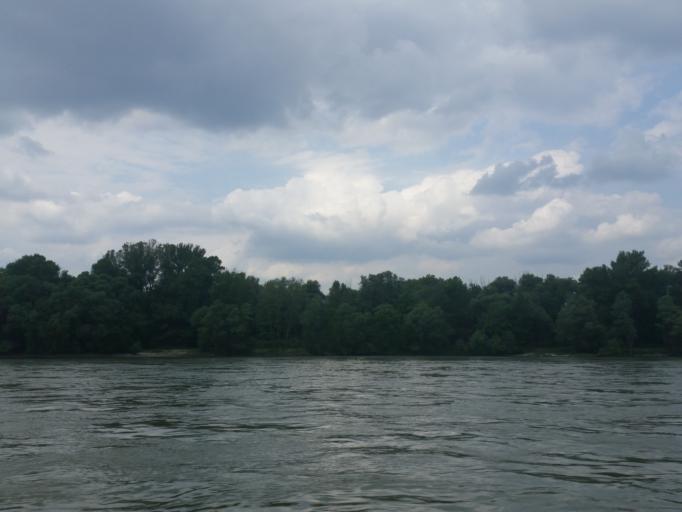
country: AT
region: Lower Austria
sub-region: Politischer Bezirk Bruck an der Leitha
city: Bad Deutsch-Altenburg
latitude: 48.1452
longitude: 16.9060
